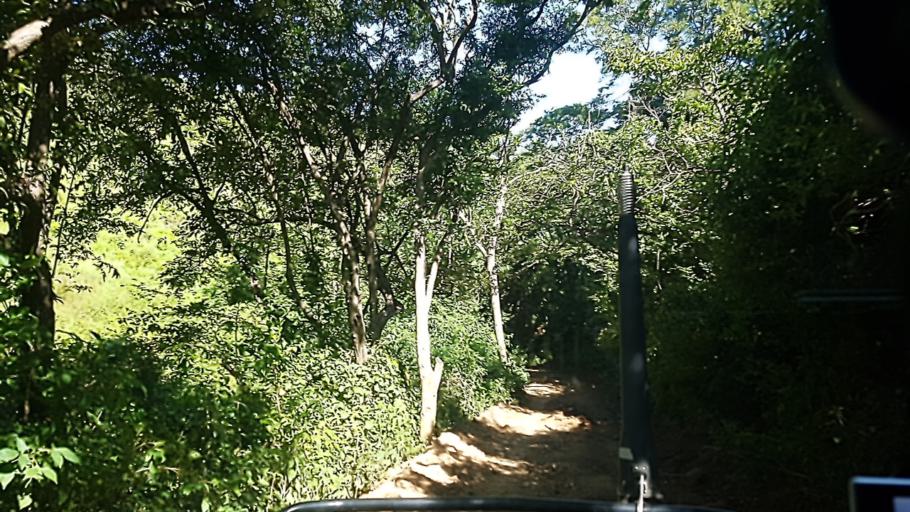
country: NI
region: Granada
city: Nandaime
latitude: 11.5667
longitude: -86.0895
